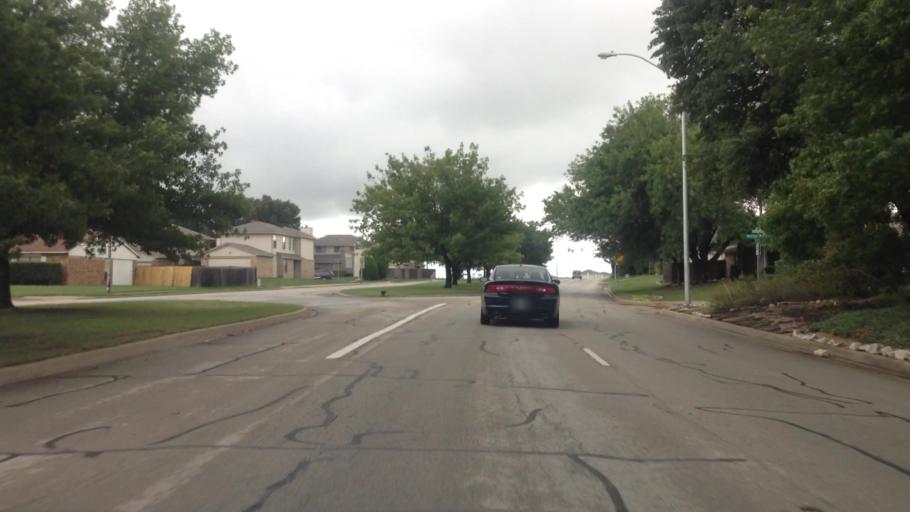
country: US
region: Texas
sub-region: Tarrant County
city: Edgecliff Village
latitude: 32.6300
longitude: -97.3878
